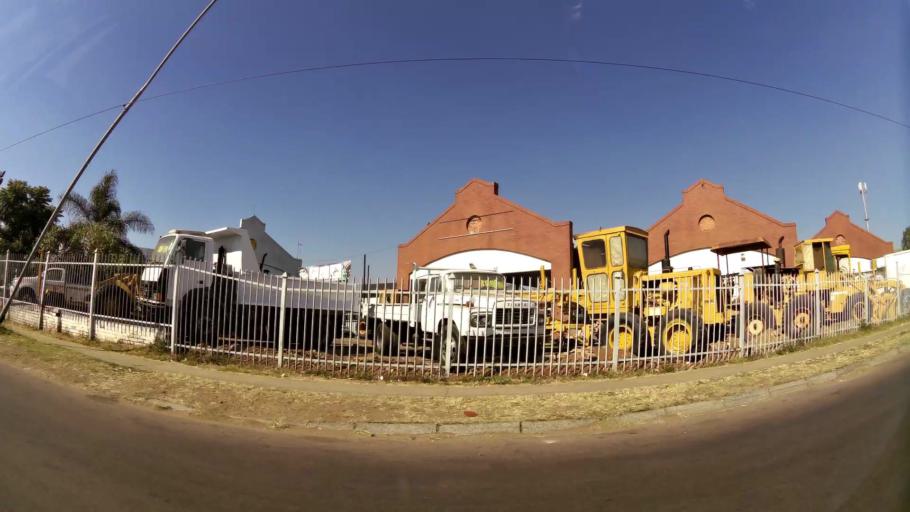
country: ZA
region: Gauteng
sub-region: City of Tshwane Metropolitan Municipality
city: Pretoria
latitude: -25.7537
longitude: 28.1741
